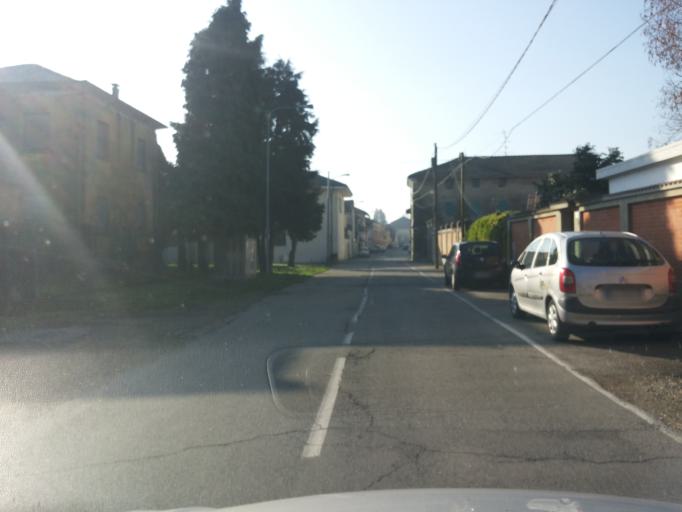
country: IT
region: Piedmont
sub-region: Provincia di Vercelli
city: Desana
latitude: 45.2705
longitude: 8.3604
